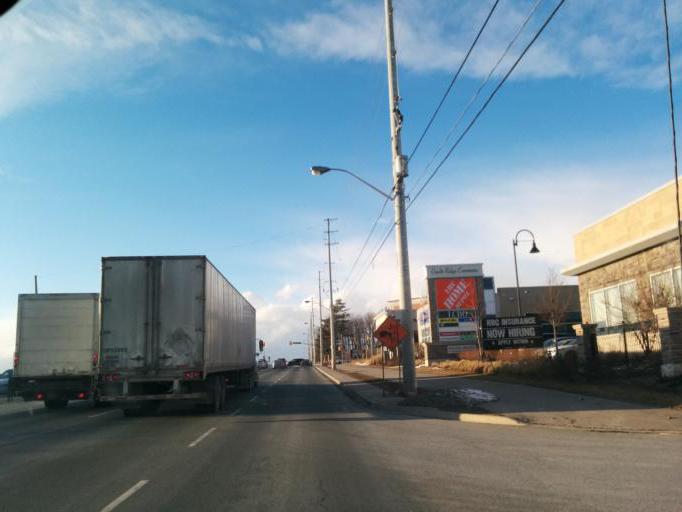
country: CA
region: Ontario
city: Brampton
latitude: 43.6573
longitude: -79.8163
